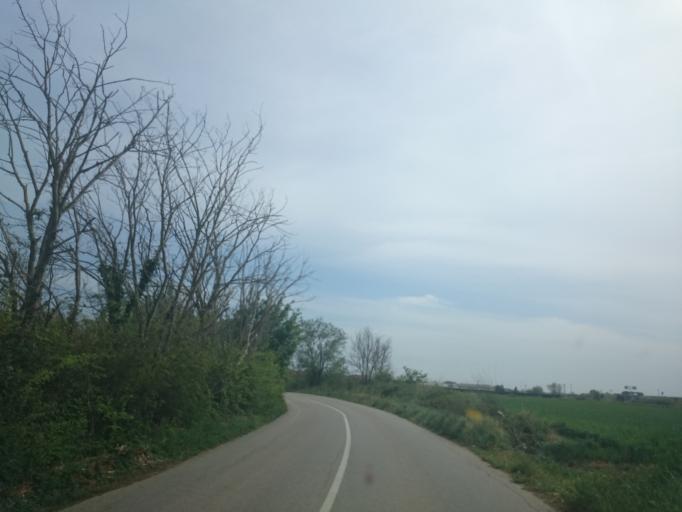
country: ES
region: Catalonia
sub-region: Provincia de Girona
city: Vilabertran
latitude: 42.2728
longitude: 2.9883
